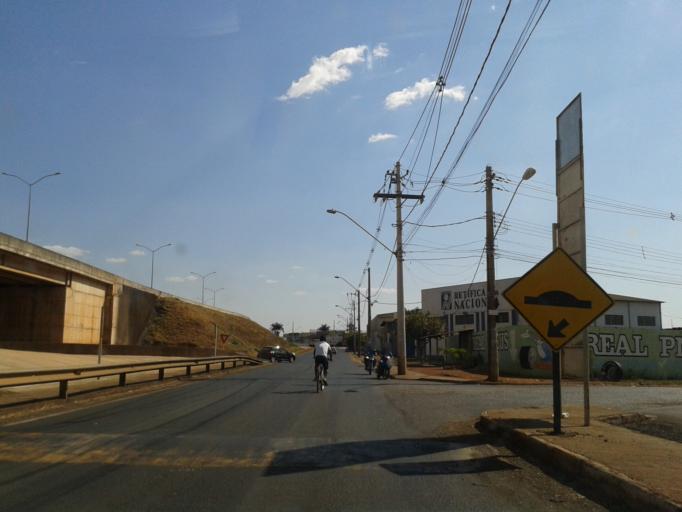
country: BR
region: Minas Gerais
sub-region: Araguari
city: Araguari
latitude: -18.6648
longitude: -48.1713
